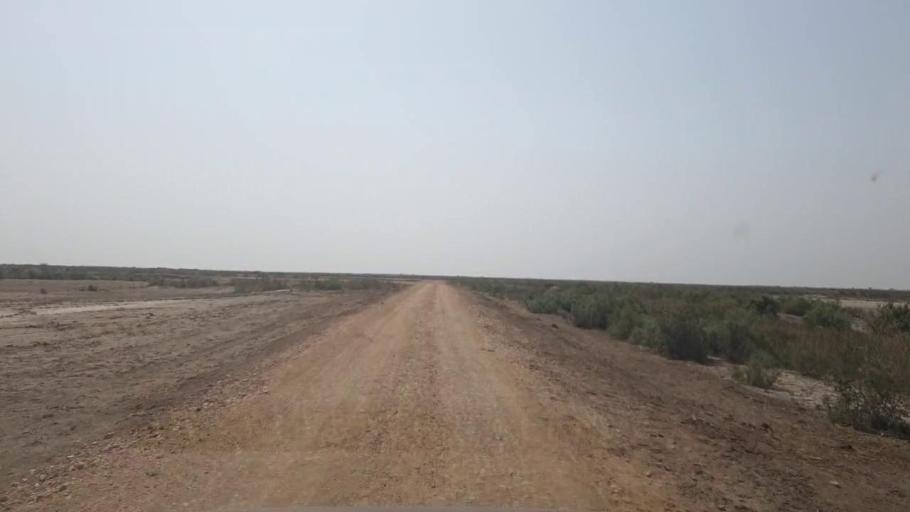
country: PK
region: Sindh
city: Jati
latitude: 24.3745
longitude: 68.6020
